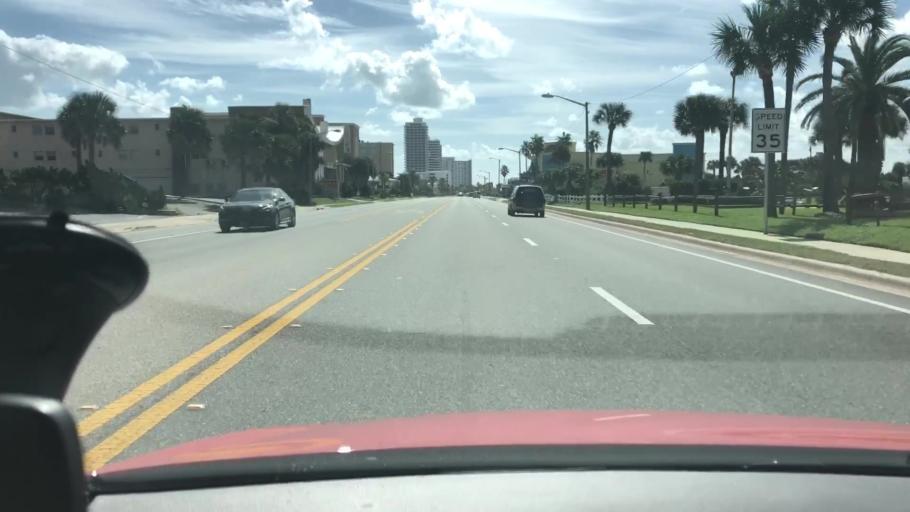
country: US
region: Florida
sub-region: Volusia County
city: Ormond Beach
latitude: 29.2751
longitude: -81.0316
